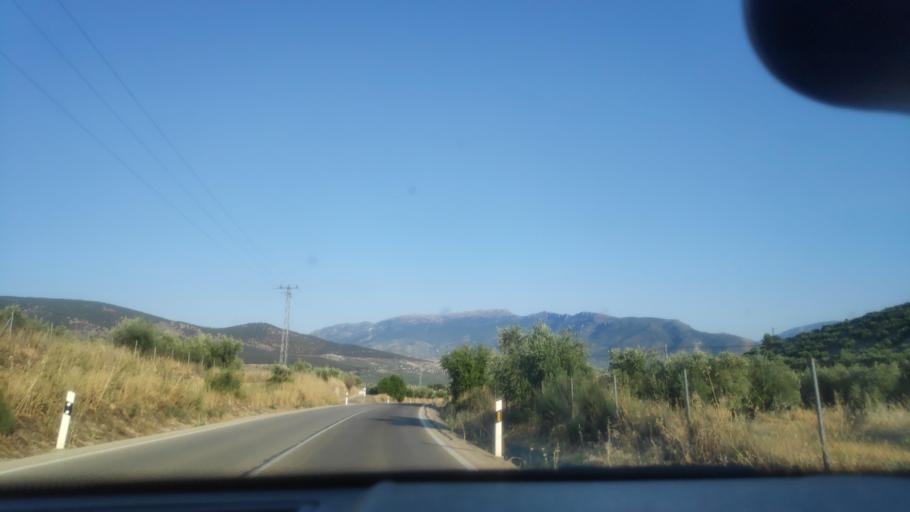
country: ES
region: Andalusia
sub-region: Provincia de Jaen
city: Jaen
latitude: 37.7460
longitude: -3.7793
